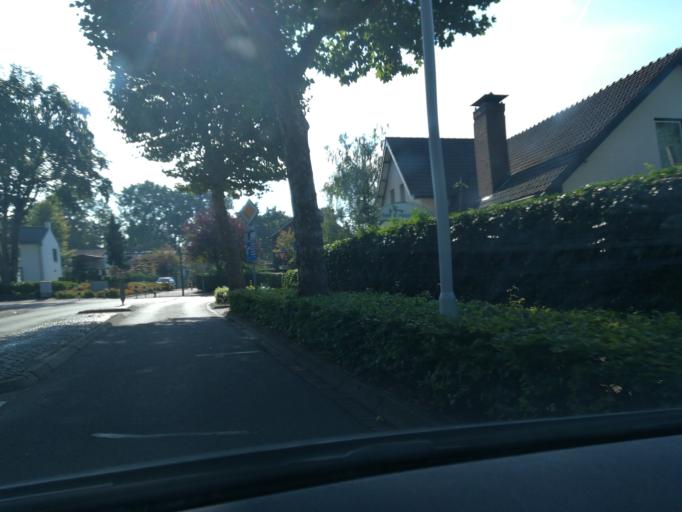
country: NL
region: North Brabant
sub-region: Gemeente Waalre
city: Waalre
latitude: 51.3945
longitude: 5.4690
